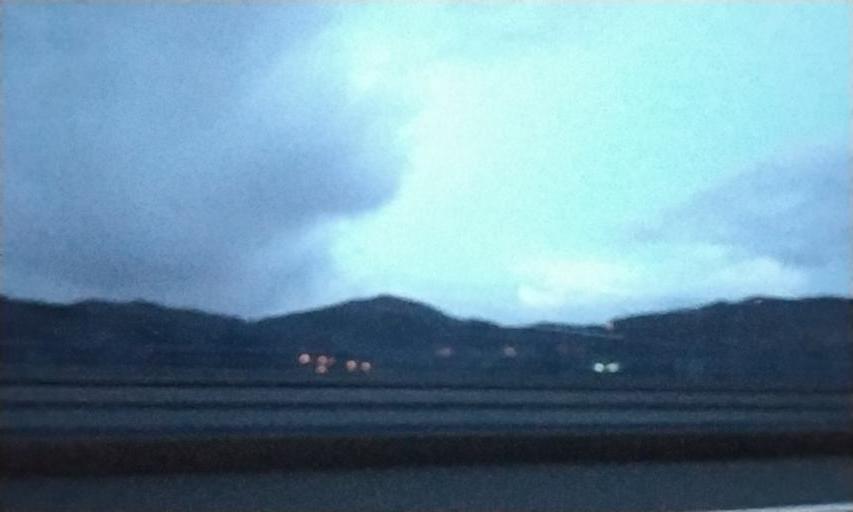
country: PT
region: Braga
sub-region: Vila Nova de Famalicao
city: Joane
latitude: 41.4924
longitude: -8.4127
